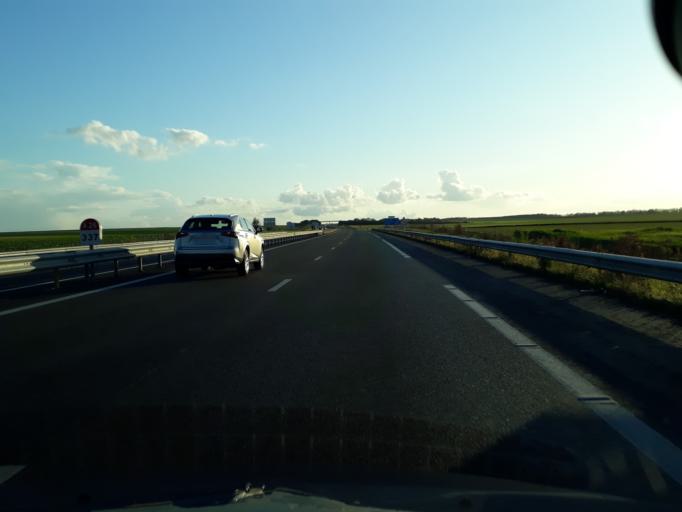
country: FR
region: Champagne-Ardenne
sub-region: Departement de l'Aube
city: Mailly-le-Camp
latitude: 48.7224
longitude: 4.2182
